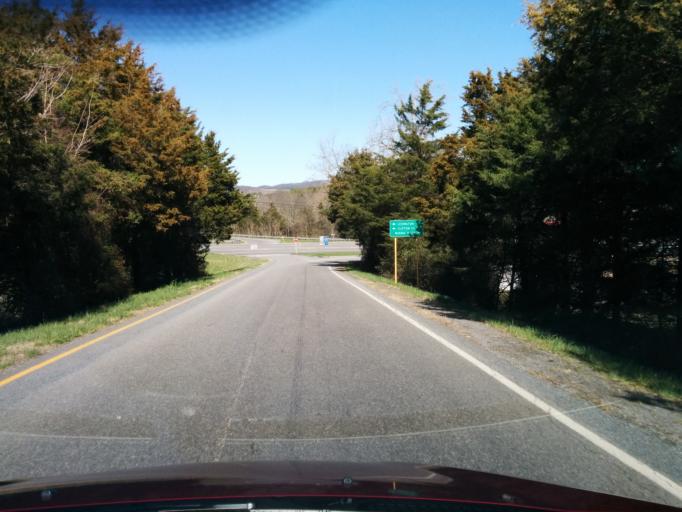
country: US
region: Virginia
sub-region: City of Lexington
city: Lexington
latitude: 37.7766
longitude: -79.4348
